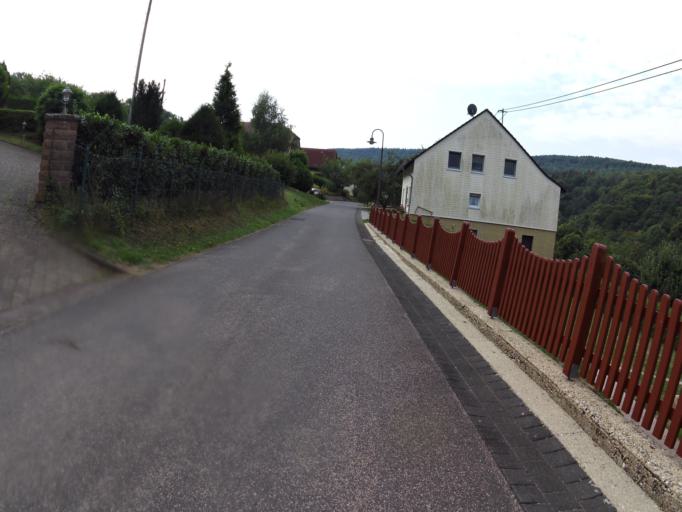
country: DE
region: Rheinland-Pfalz
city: Metterich
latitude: 49.9645
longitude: 6.5891
